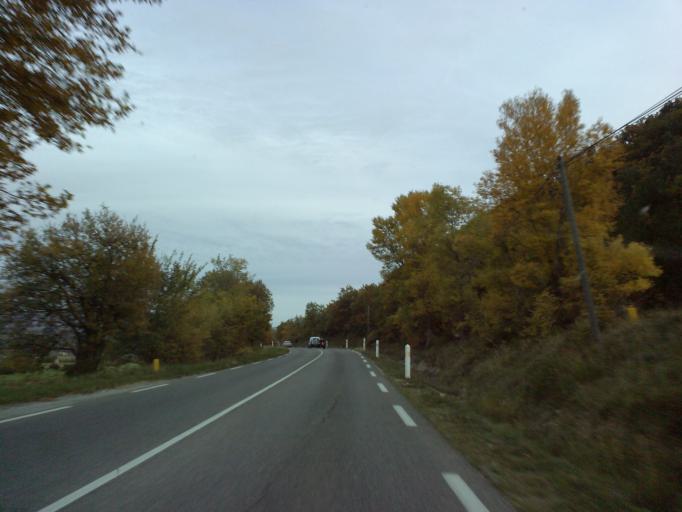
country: FR
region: Provence-Alpes-Cote d'Azur
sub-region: Departement des Alpes-de-Haute-Provence
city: Peipin
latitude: 44.1533
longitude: 5.9540
